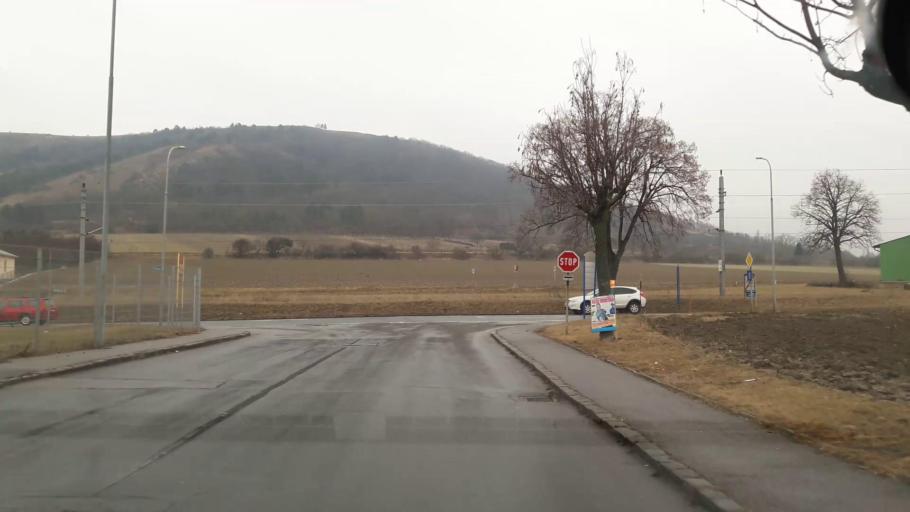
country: AT
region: Lower Austria
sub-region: Politischer Bezirk Bruck an der Leitha
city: Hainburg an der Donau
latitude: 48.1460
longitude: 16.9575
